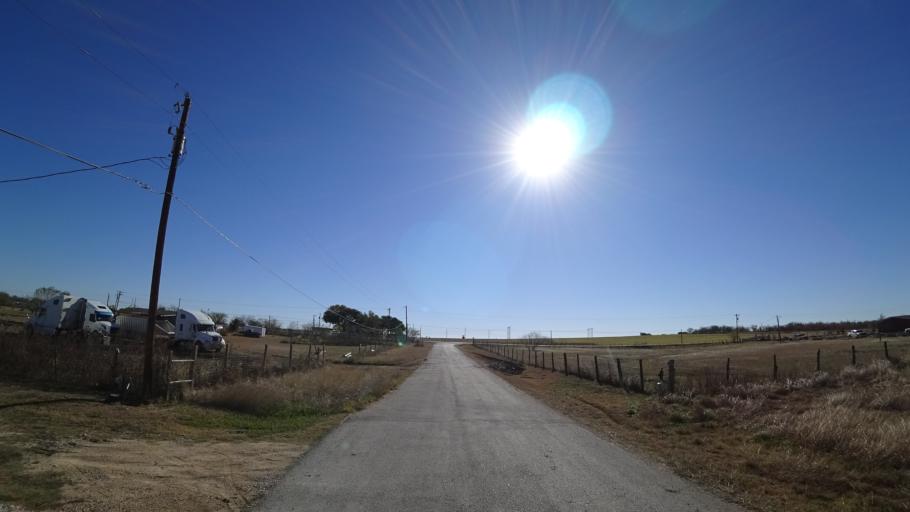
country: US
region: Texas
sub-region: Travis County
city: Onion Creek
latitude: 30.1028
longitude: -97.6807
